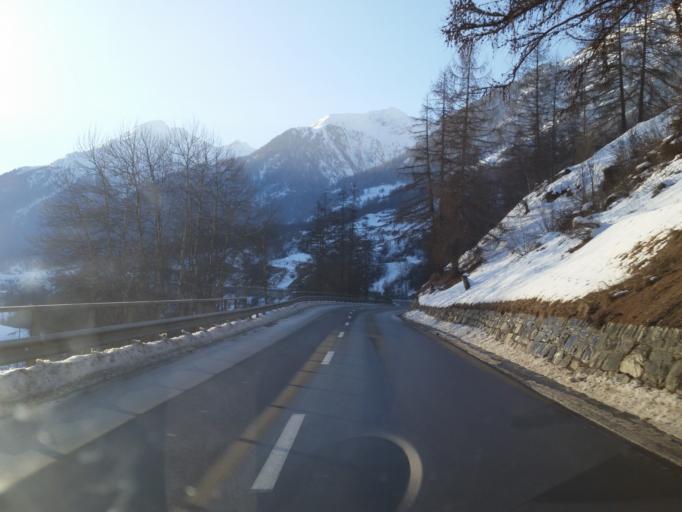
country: CH
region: Grisons
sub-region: Inn District
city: Zernez
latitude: 46.7714
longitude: 10.1383
